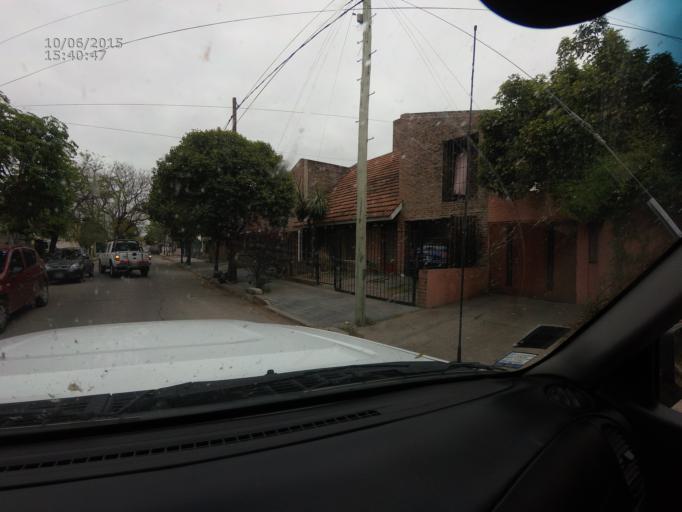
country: AR
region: Cordoba
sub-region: Departamento de Capital
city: Cordoba
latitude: -31.3645
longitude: -64.2265
